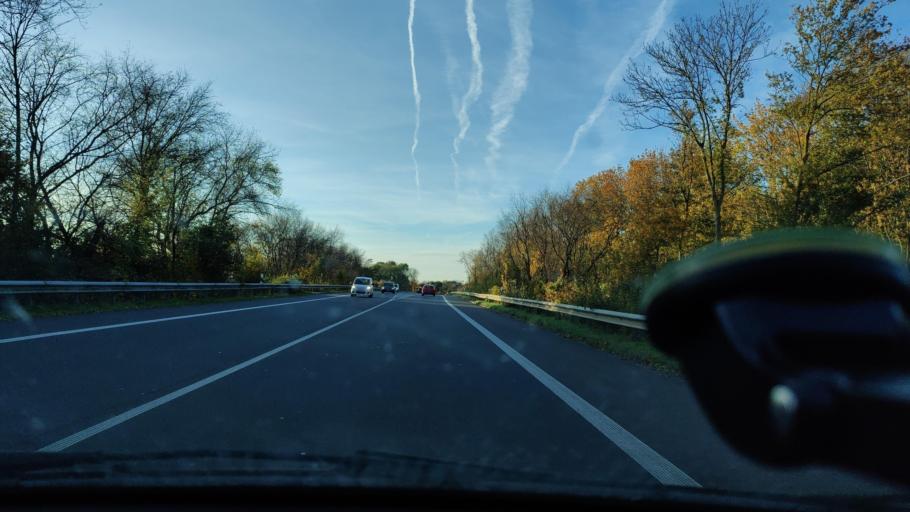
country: DE
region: North Rhine-Westphalia
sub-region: Regierungsbezirk Dusseldorf
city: Monchengladbach
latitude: 51.2323
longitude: 6.4576
